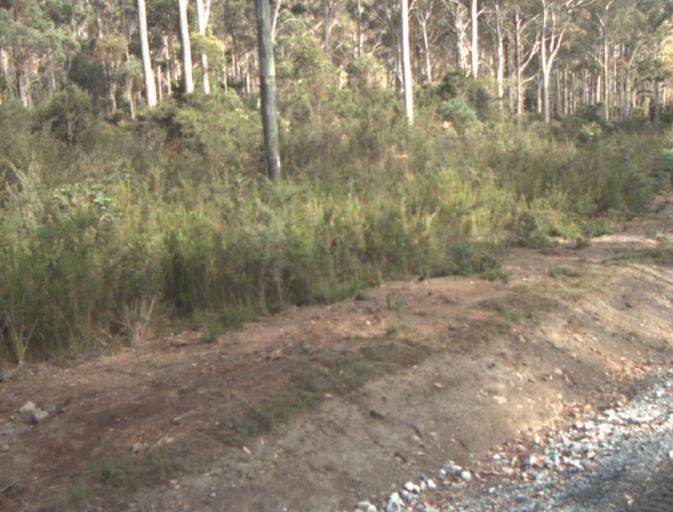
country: AU
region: Tasmania
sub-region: Launceston
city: Mayfield
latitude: -41.3073
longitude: 147.1990
